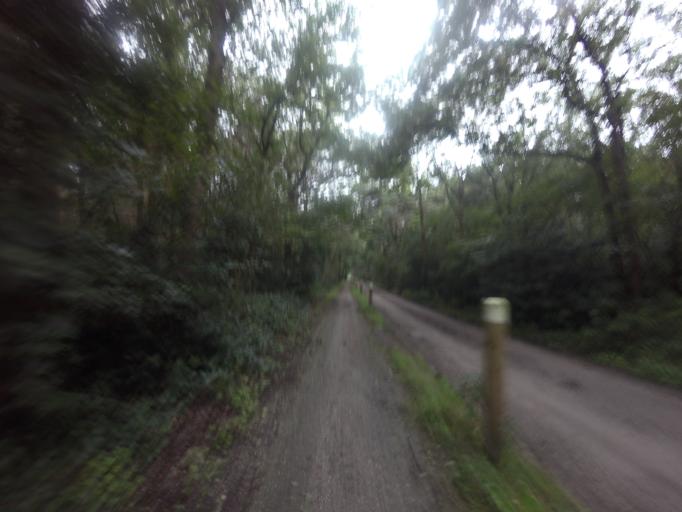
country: NL
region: Friesland
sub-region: Gemeente Heerenveen
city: Nieuwehorne
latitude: 52.9530
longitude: 6.1017
